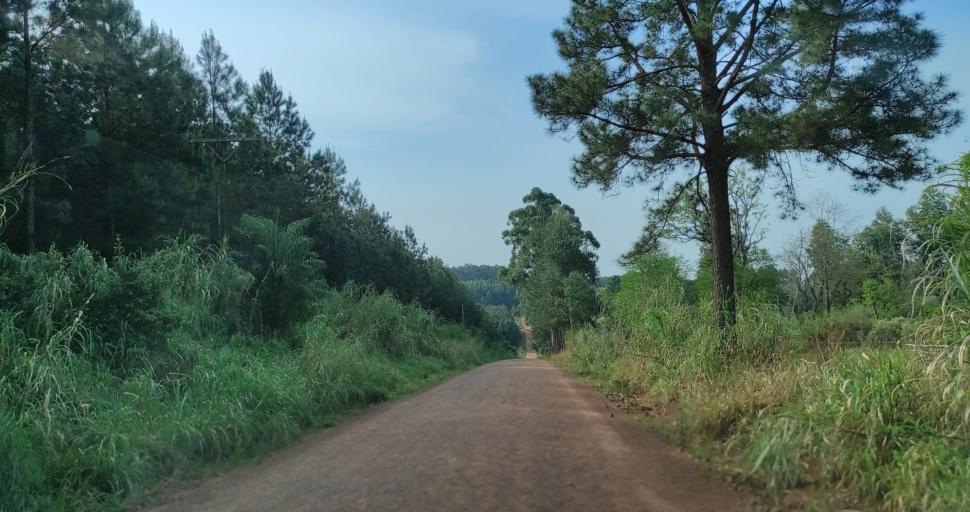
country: AR
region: Misiones
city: Garuhape
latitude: -26.8659
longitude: -55.0050
